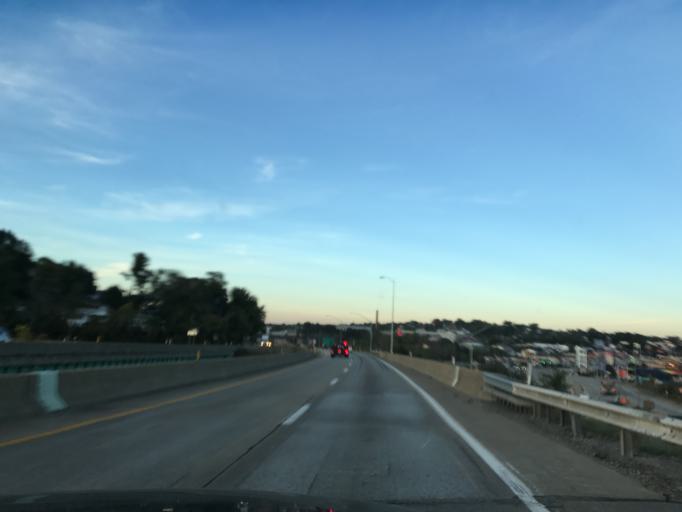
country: US
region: Pennsylvania
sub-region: Washington County
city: Wolfdale
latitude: 40.1614
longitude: -80.2784
